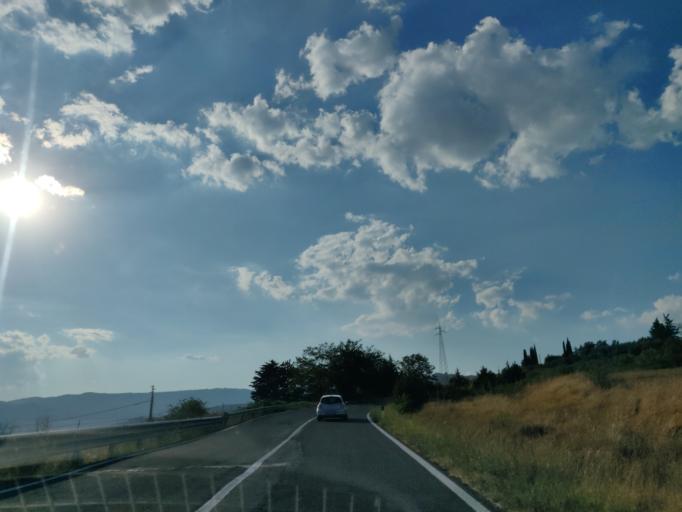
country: IT
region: Tuscany
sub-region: Provincia di Siena
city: Piancastagnaio
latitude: 42.8294
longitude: 11.7193
